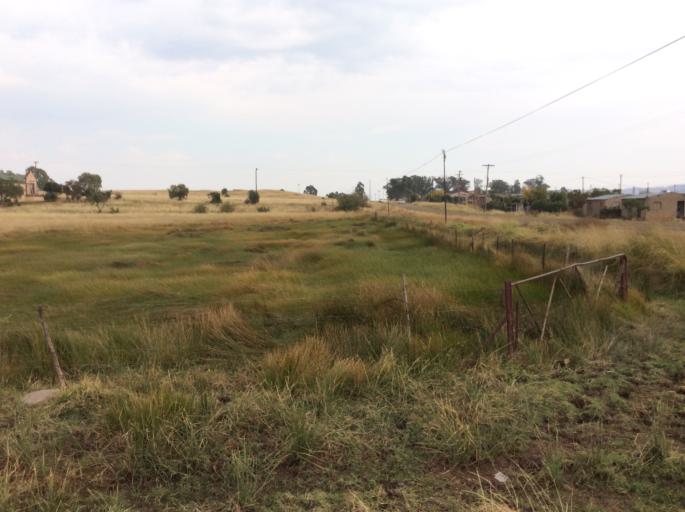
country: LS
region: Mafeteng
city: Mafeteng
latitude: -29.9867
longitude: 27.0106
